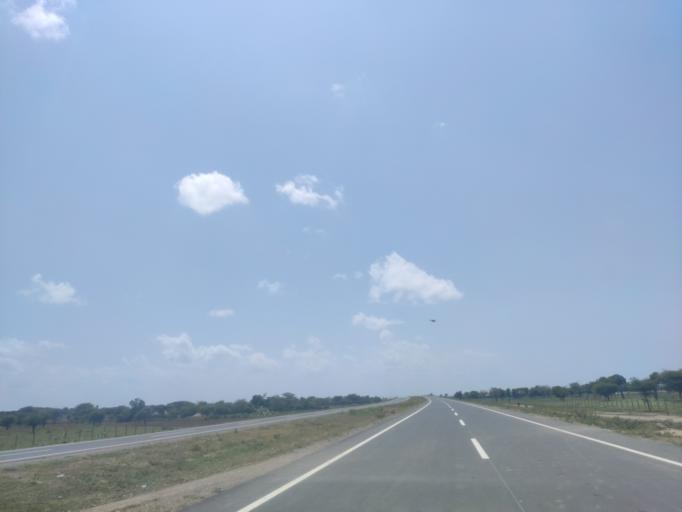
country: ET
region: Oromiya
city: Mojo
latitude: 8.3484
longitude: 38.9802
